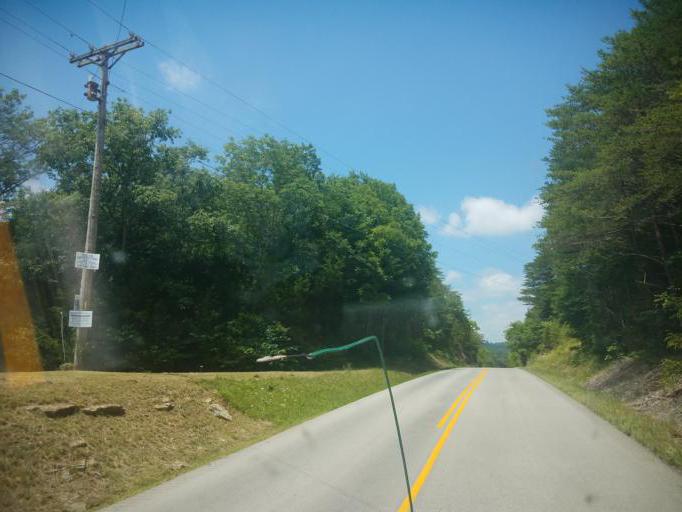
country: US
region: Kentucky
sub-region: Edmonson County
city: Brownsville
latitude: 37.3351
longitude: -86.1257
